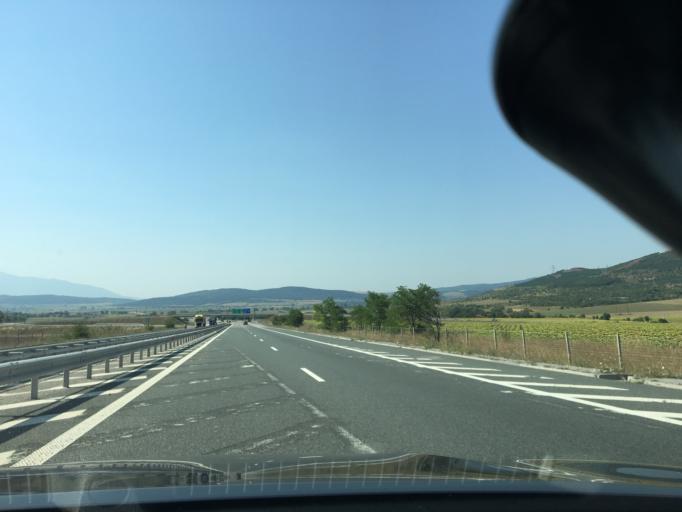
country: BG
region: Kyustendil
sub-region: Obshtina Bobovdol
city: Bobovdol
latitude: 42.4573
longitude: 23.1125
